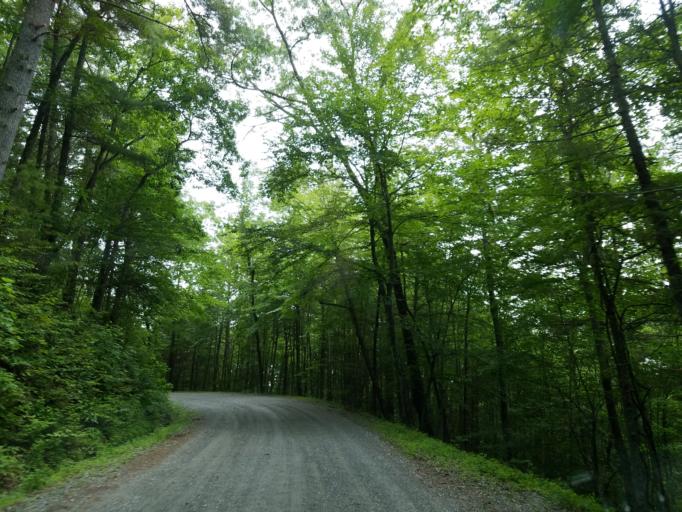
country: US
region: Georgia
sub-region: Fannin County
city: Blue Ridge
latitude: 34.8157
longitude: -84.2411
